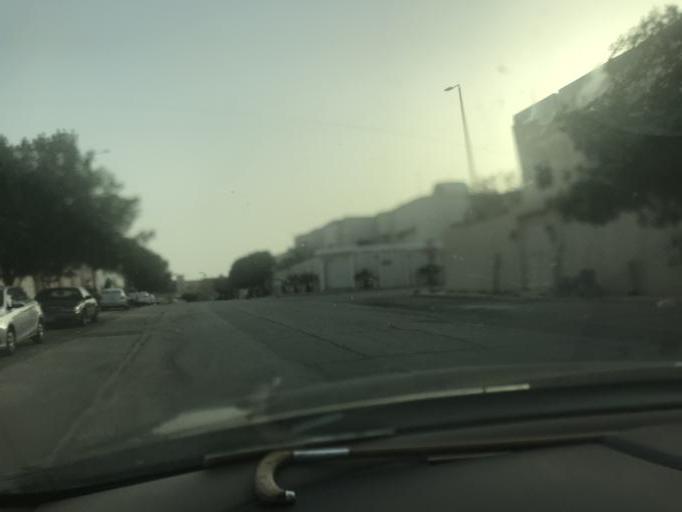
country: SA
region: Ar Riyad
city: Riyadh
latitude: 24.7406
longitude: 46.7549
